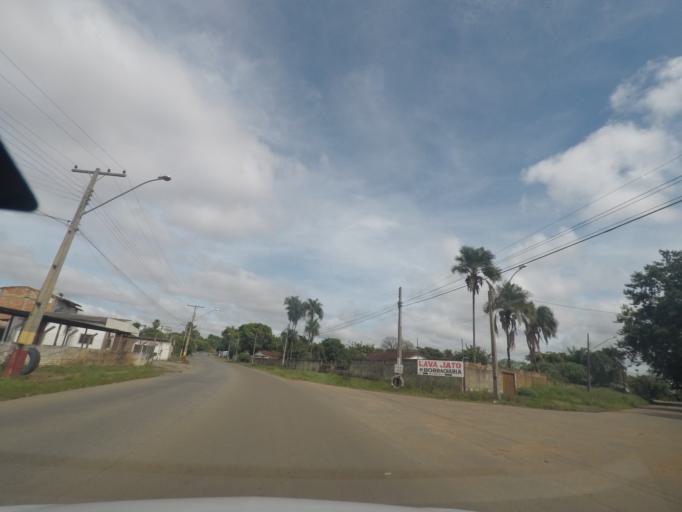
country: BR
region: Goias
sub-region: Goiania
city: Goiania
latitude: -16.6733
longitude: -49.2020
